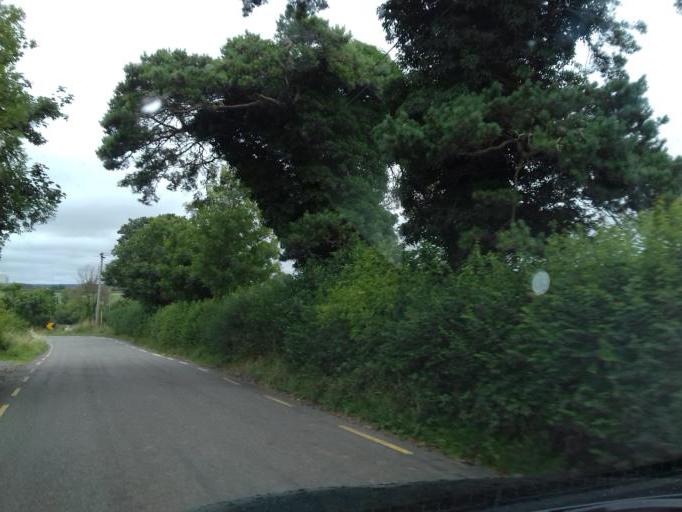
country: IE
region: Leinster
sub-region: County Carlow
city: Bagenalstown
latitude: 52.6250
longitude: -7.0415
